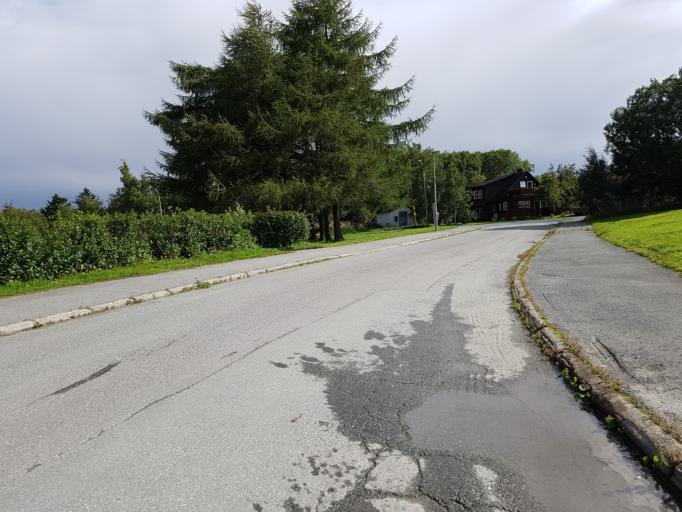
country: NO
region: Sor-Trondelag
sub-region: Trondheim
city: Trondheim
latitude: 63.4159
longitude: 10.4837
